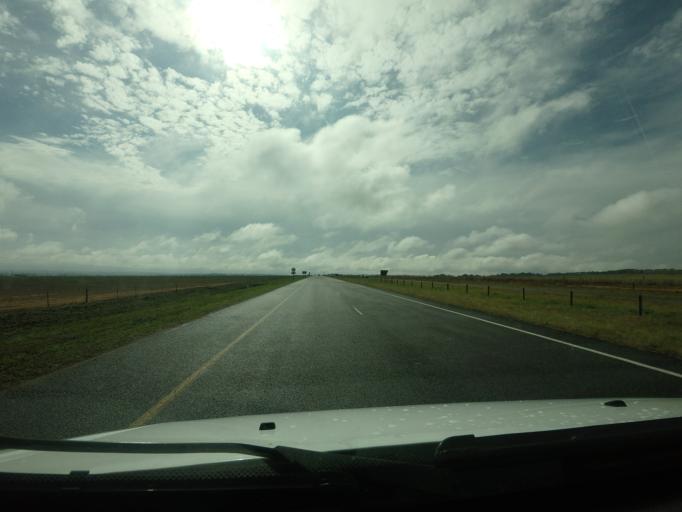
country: ZA
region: Gauteng
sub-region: City of Tshwane Metropolitan Municipality
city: Cullinan
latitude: -25.7975
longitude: 28.5276
